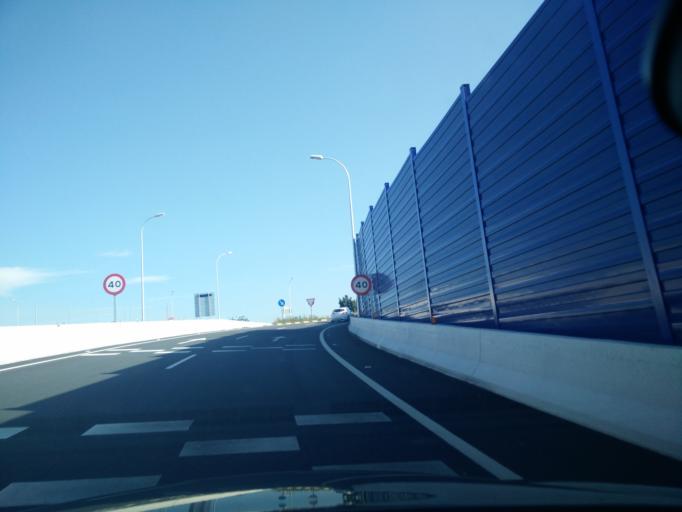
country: ES
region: Galicia
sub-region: Provincia da Coruna
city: Culleredo
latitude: 43.3232
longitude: -8.4109
